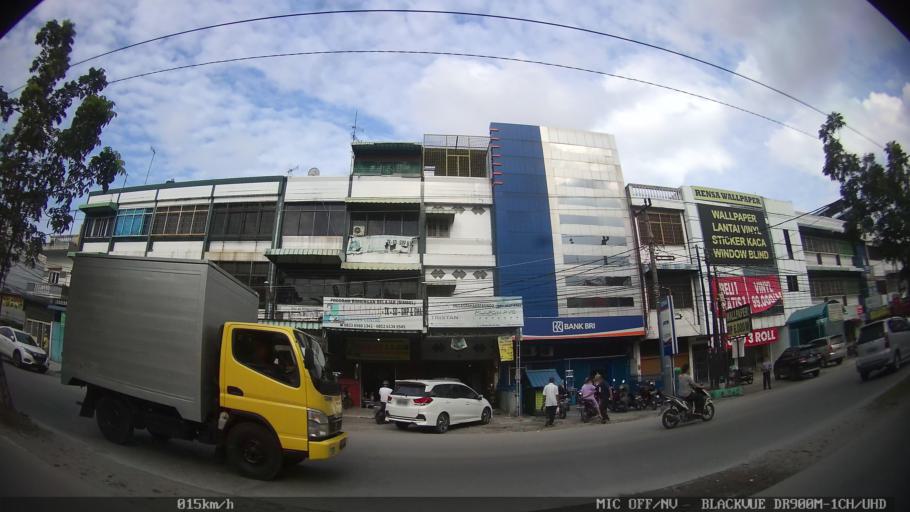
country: ID
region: North Sumatra
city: Medan
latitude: 3.6181
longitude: 98.6807
